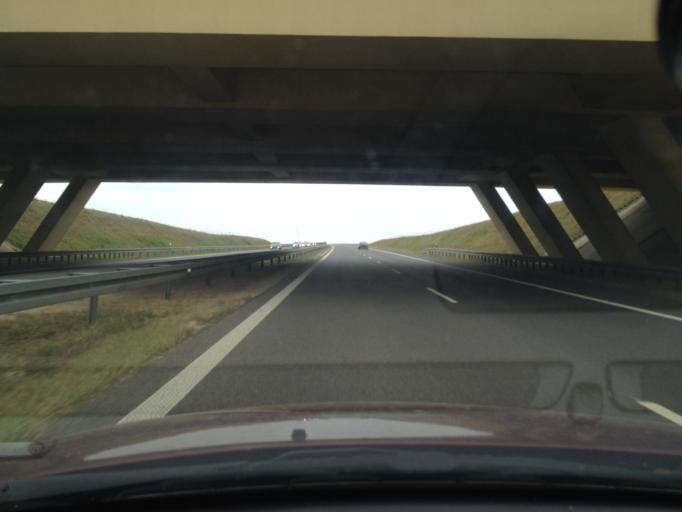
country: PL
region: West Pomeranian Voivodeship
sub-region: Powiat pyrzycki
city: Kozielice
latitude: 53.0666
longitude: 14.8622
